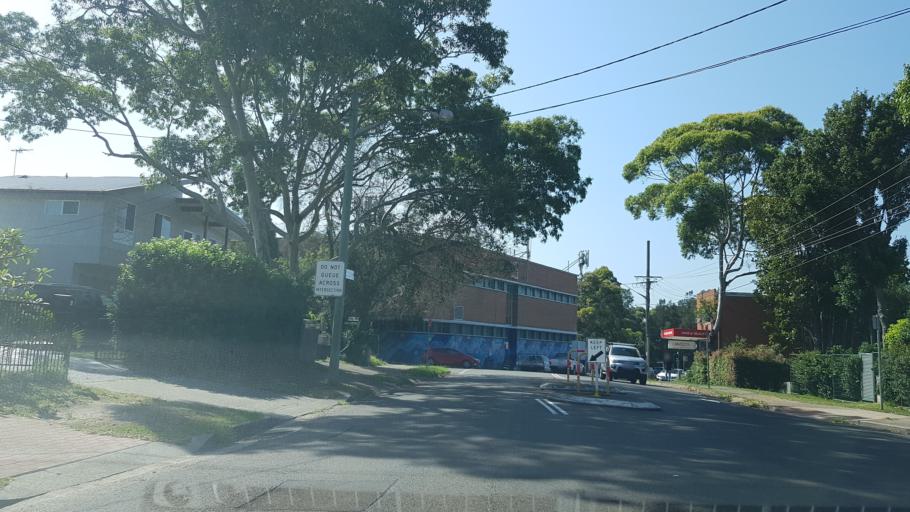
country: AU
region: New South Wales
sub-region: Warringah
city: Dee Why
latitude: -33.7439
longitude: 151.2936
